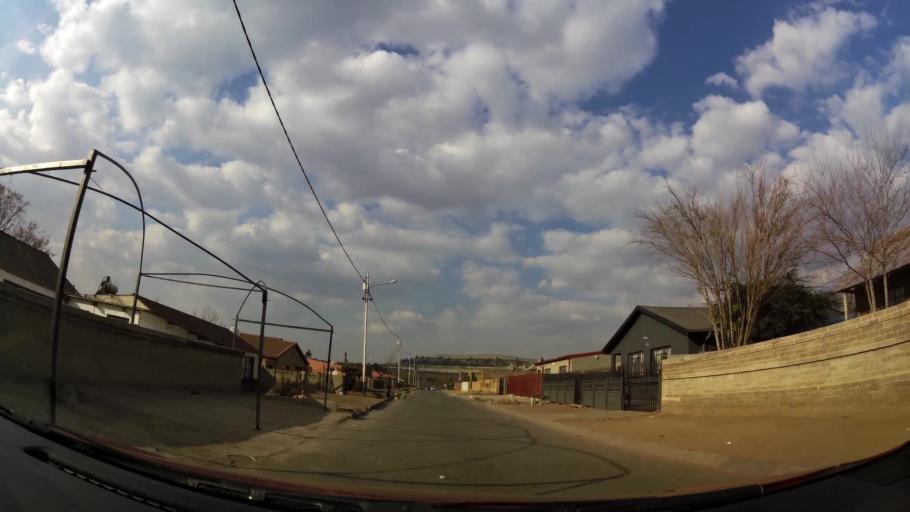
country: ZA
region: Gauteng
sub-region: City of Johannesburg Metropolitan Municipality
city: Soweto
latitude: -26.2264
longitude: 27.9329
